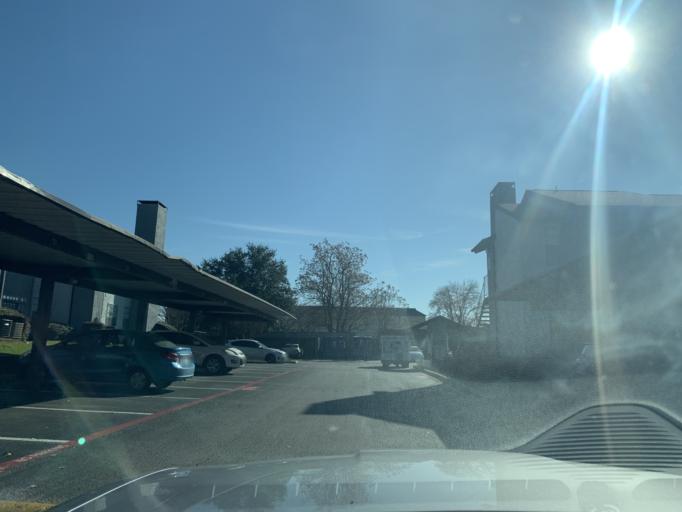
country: US
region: Texas
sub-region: Tarrant County
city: Bedford
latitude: 32.8324
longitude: -97.1404
